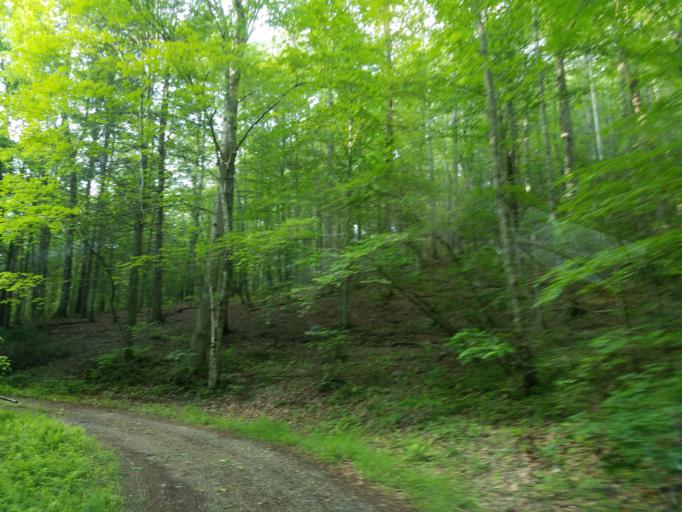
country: US
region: Georgia
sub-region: Union County
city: Blairsville
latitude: 34.7430
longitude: -84.0324
